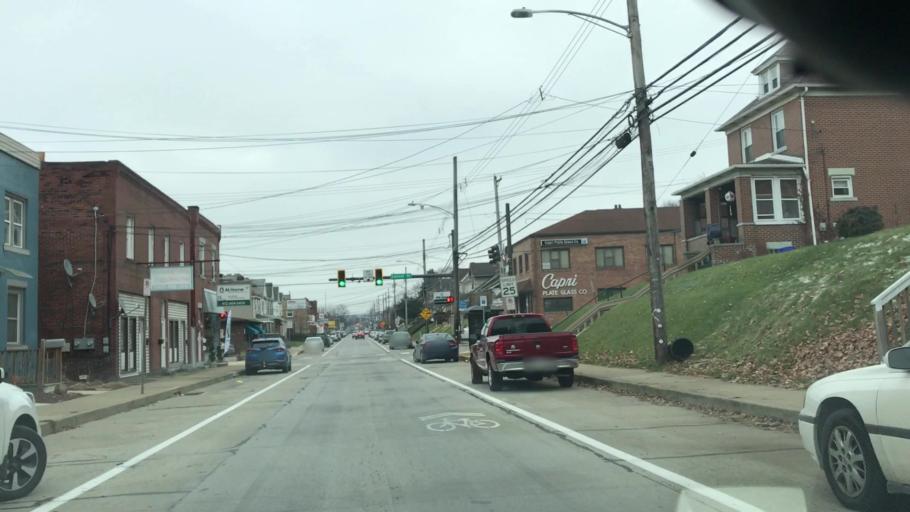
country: US
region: Pennsylvania
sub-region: Allegheny County
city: Coraopolis
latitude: 40.5206
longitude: -80.1724
